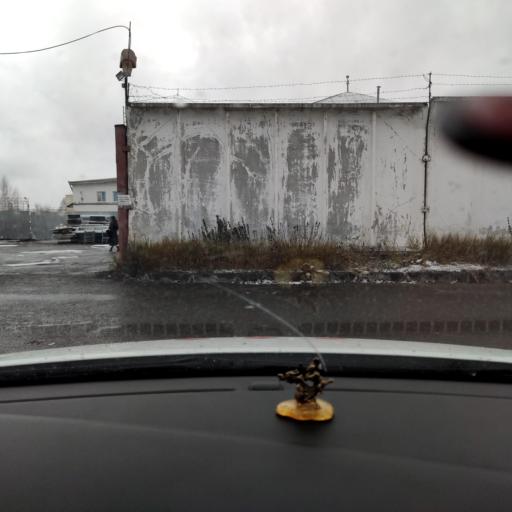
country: RU
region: Tatarstan
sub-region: Gorod Kazan'
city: Kazan
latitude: 55.7334
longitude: 49.1298
